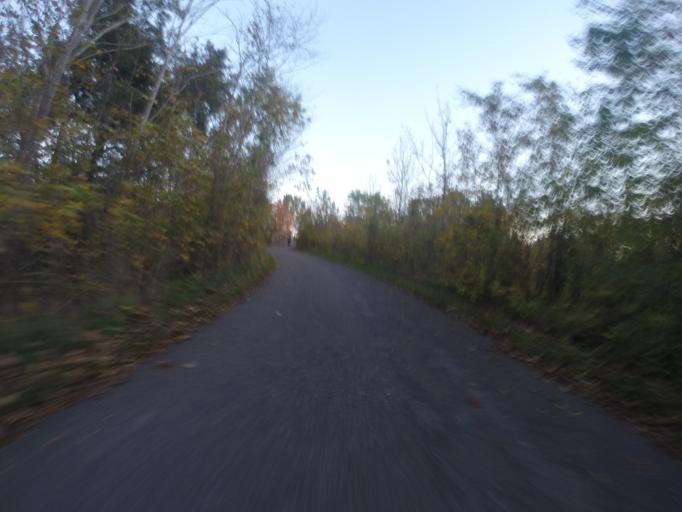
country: DK
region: Capital Region
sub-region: Hoje-Taastrup Kommune
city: Taastrup
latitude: 55.6606
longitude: 12.3225
